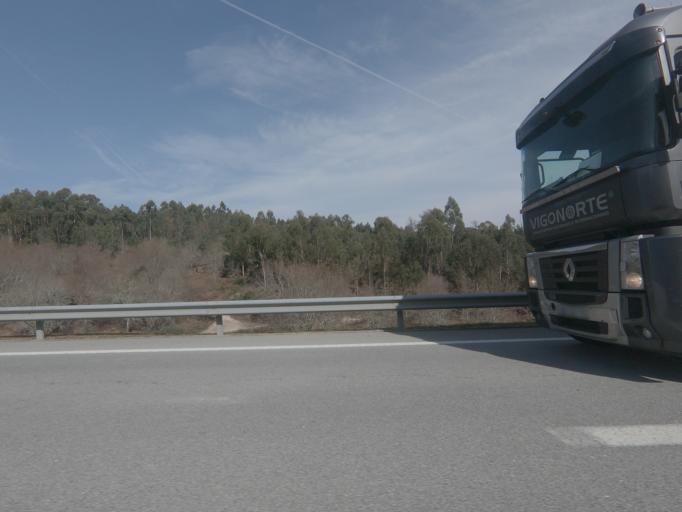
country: PT
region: Viseu
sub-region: Viseu
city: Viseu
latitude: 40.6311
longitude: -7.9733
